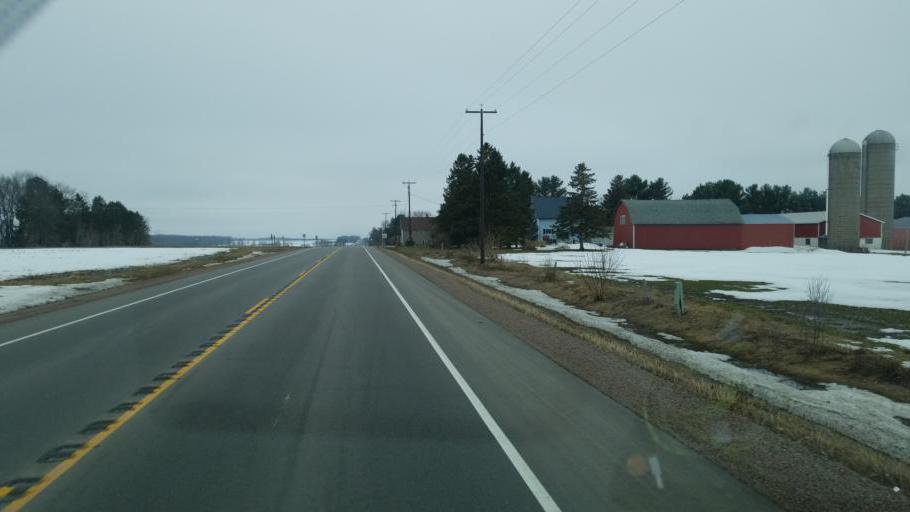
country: US
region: Wisconsin
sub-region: Marathon County
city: Spencer
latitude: 44.6563
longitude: -90.2971
